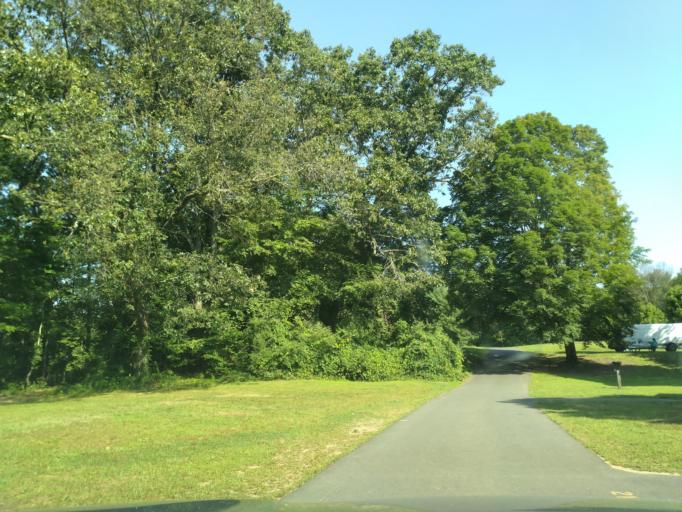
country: US
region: Connecticut
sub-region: New Haven County
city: Southbury
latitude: 41.4196
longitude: -73.2042
